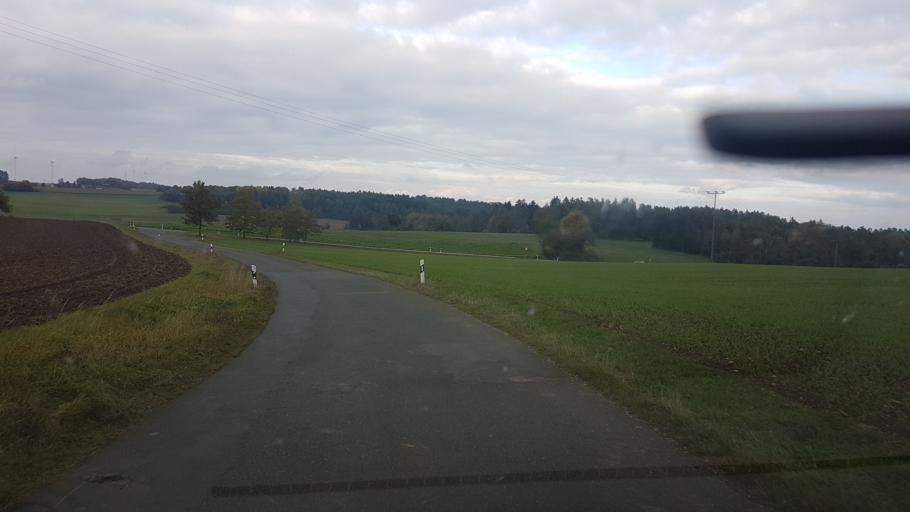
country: DE
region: Bavaria
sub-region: Upper Franconia
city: Poxdorf
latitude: 49.8943
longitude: 11.0929
